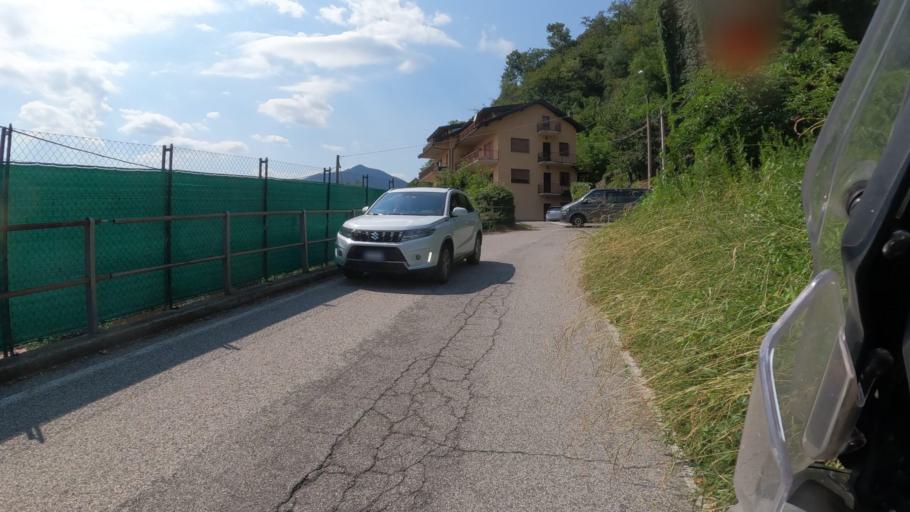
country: IT
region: Lombardy
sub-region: Provincia di Varese
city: Maccagno
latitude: 46.0459
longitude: 8.7423
